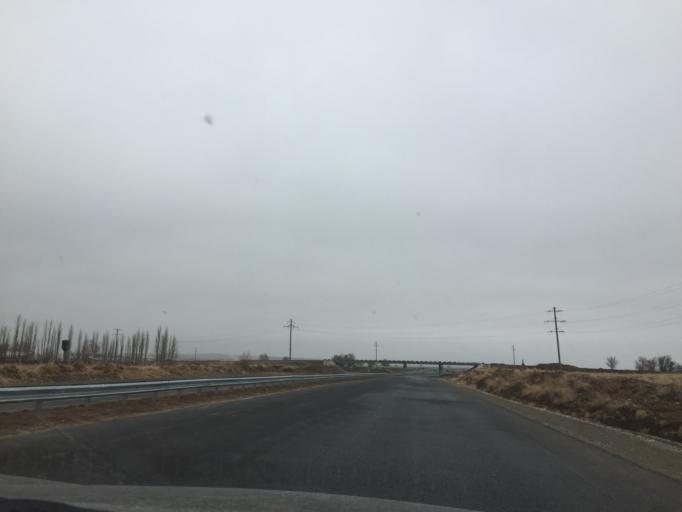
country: KZ
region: Ongtustik Qazaqstan
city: Turar Ryskulov
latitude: 42.5233
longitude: 70.3156
